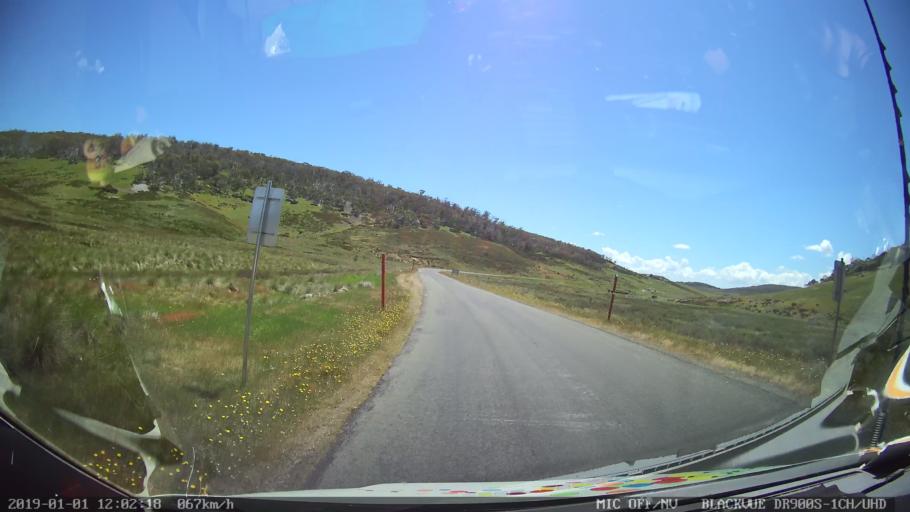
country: AU
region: New South Wales
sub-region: Snowy River
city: Jindabyne
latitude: -35.8735
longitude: 148.4754
